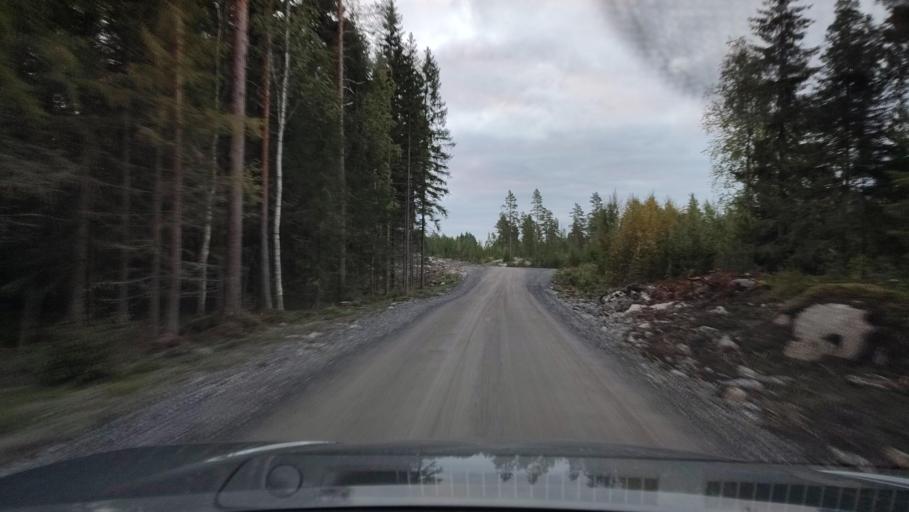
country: FI
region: Ostrobothnia
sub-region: Sydosterbotten
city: Kristinestad
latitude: 62.1899
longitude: 21.5363
